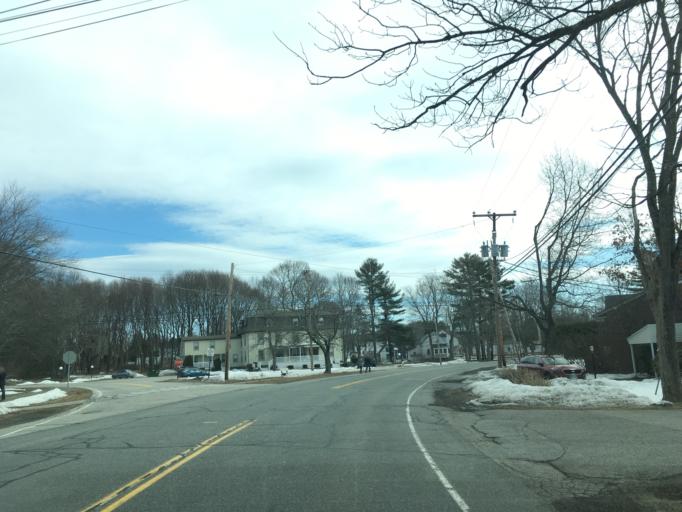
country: US
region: New Hampshire
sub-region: Rockingham County
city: Hampton
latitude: 42.9370
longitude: -70.8310
